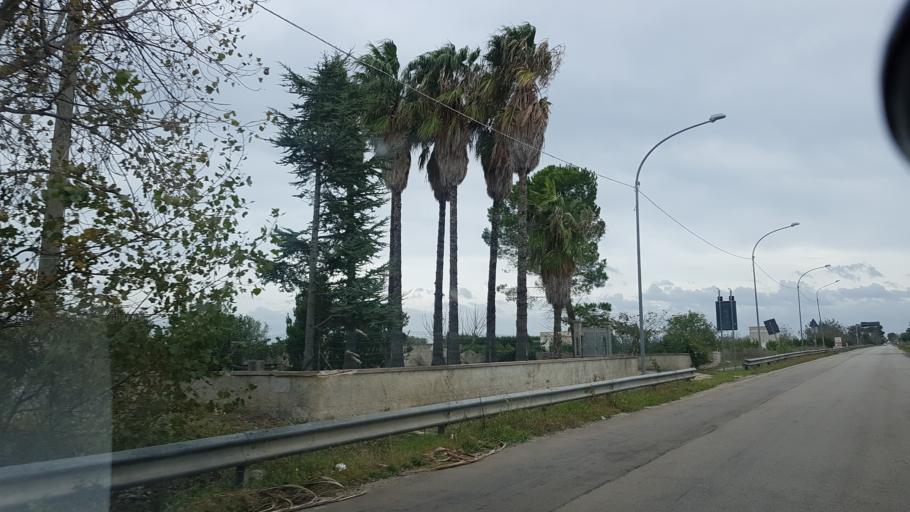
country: IT
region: Apulia
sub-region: Provincia di Brindisi
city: San Pancrazio Salentino
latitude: 40.4158
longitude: 17.8488
